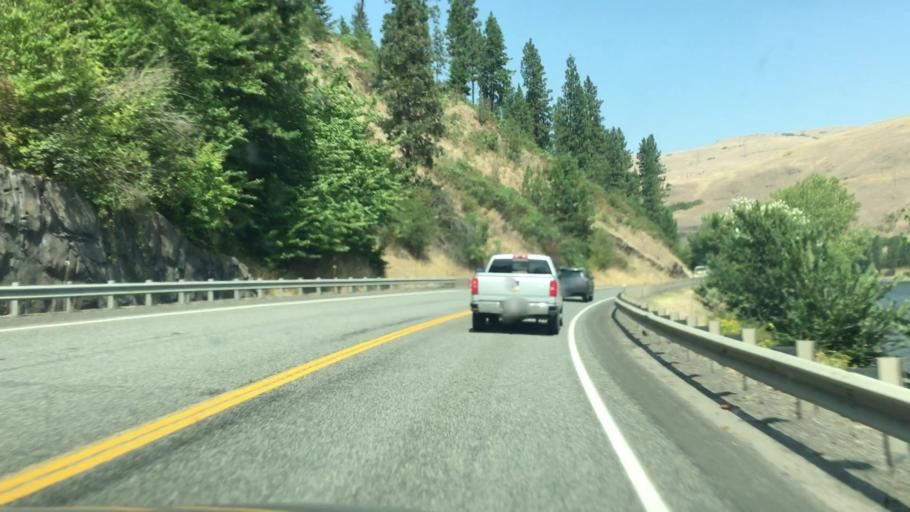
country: US
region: Idaho
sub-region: Nez Perce County
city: Lapwai
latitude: 46.5087
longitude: -116.5790
